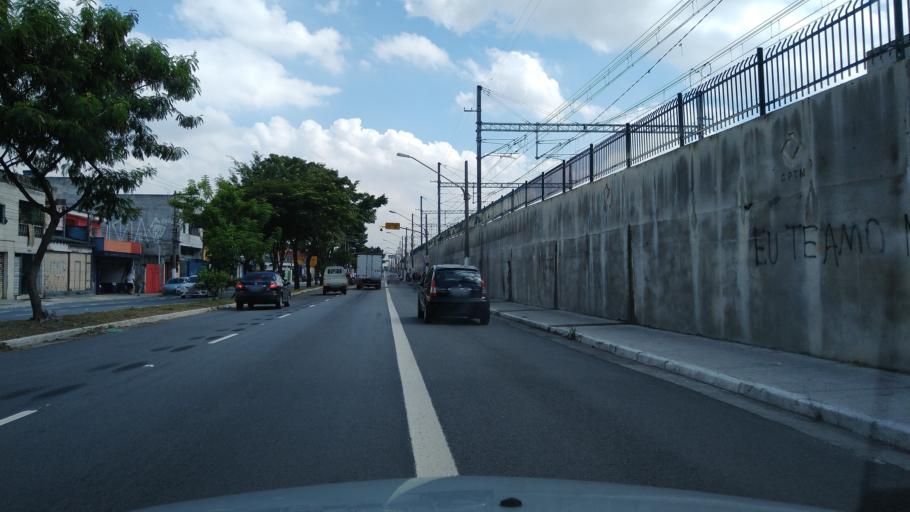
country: BR
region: Sao Paulo
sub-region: Guarulhos
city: Guarulhos
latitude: -23.5018
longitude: -46.5338
